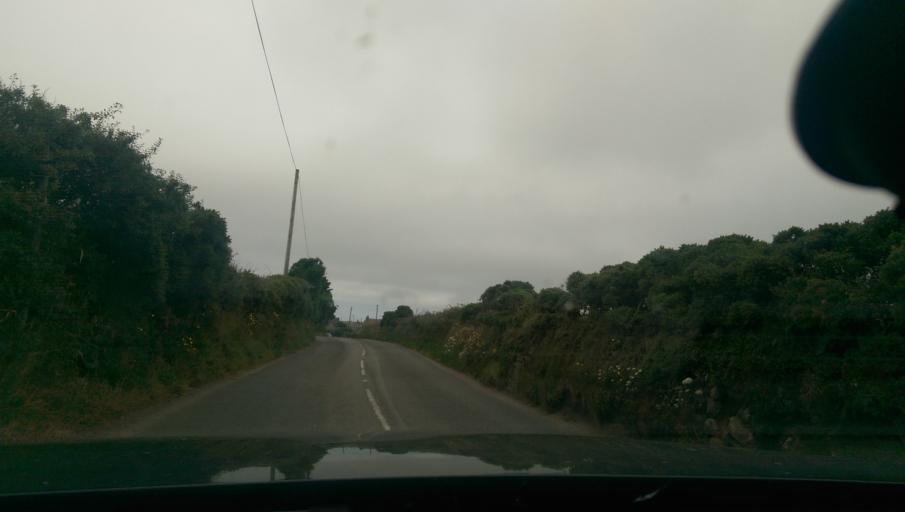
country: GB
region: England
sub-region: Cornwall
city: Saint Just
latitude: 50.1098
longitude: -5.6754
